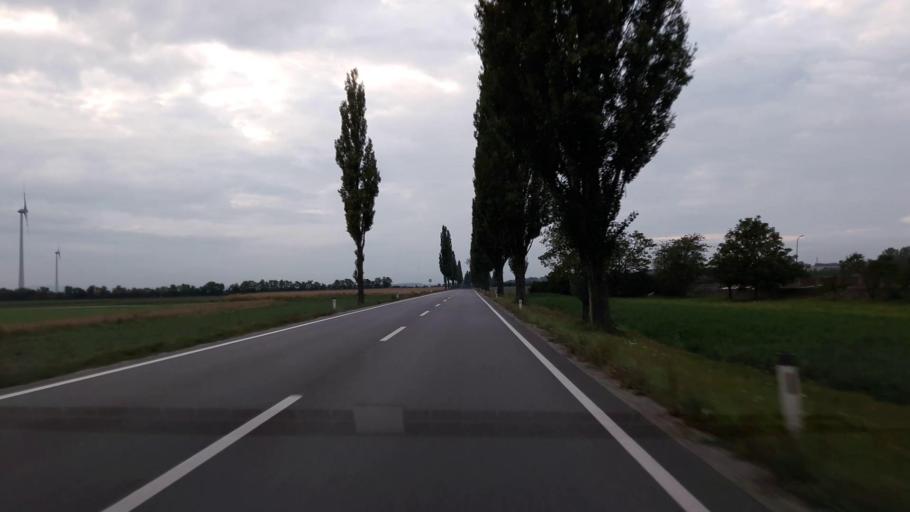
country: AT
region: Lower Austria
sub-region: Politischer Bezirk Bruck an der Leitha
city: Trautmannsdorf an der Leitha
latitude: 48.0400
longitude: 16.6715
